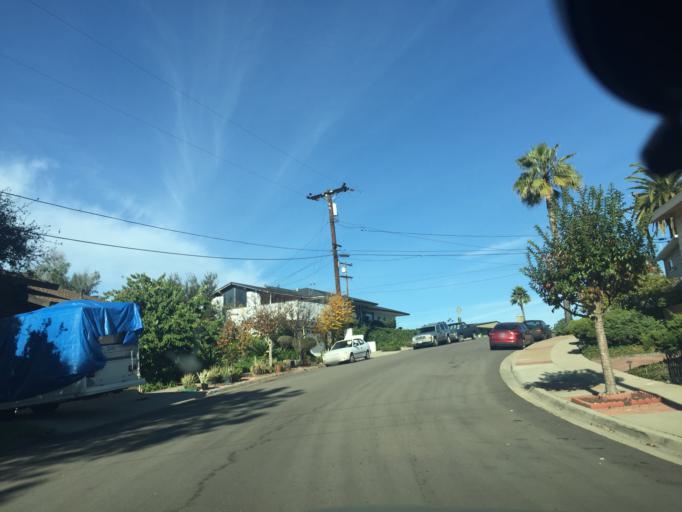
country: US
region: California
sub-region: San Diego County
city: Lemon Grove
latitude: 32.7684
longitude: -117.0821
